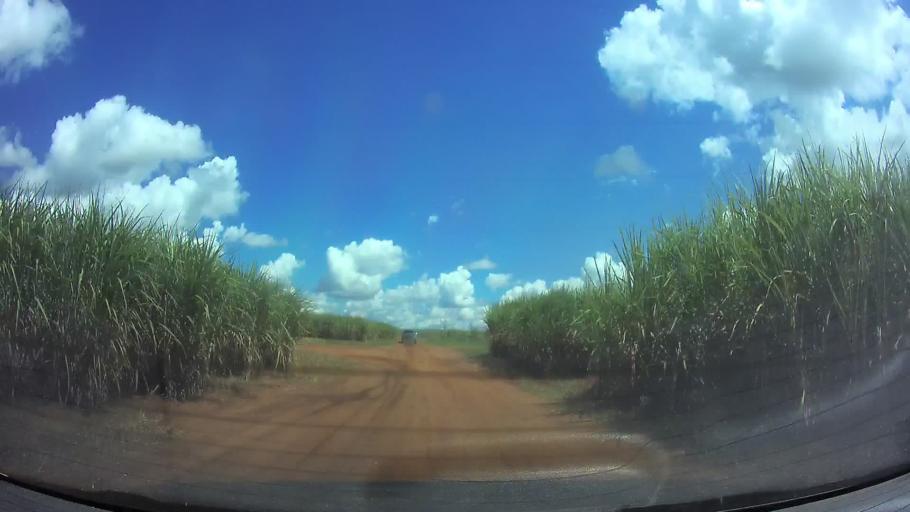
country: PY
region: Paraguari
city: La Colmena
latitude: -25.9639
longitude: -56.7627
